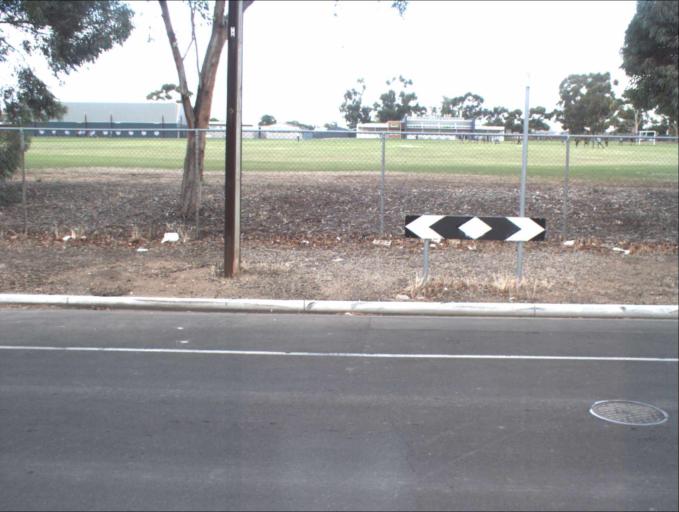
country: AU
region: South Australia
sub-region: Port Adelaide Enfield
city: Gilles Plains
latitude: -34.8486
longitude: 138.6558
